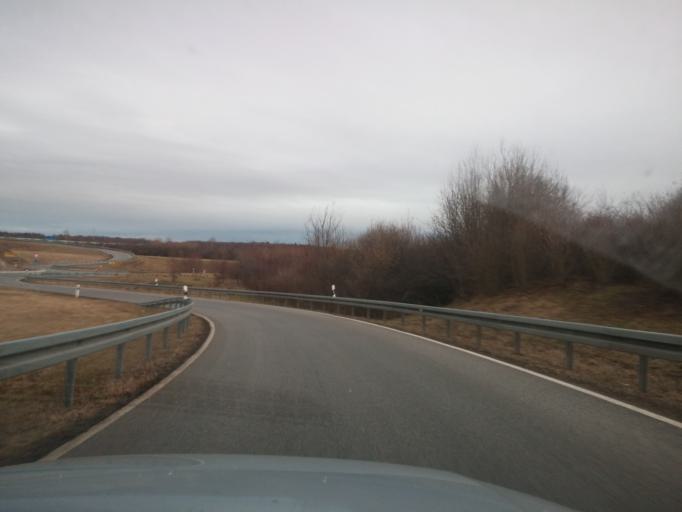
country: DE
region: Bavaria
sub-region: Upper Bavaria
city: Aschheim
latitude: 48.1881
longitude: 11.7059
